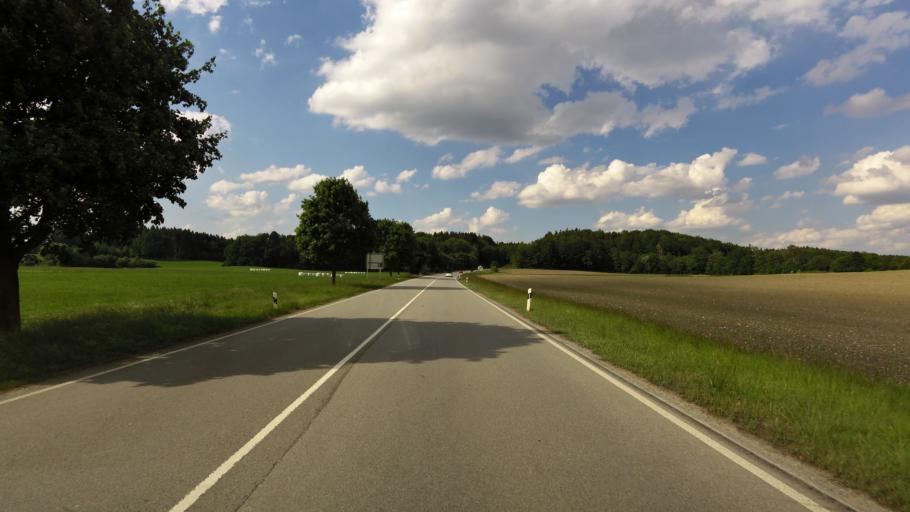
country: DE
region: Bavaria
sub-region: Upper Bavaria
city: Wasserburg am Inn
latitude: 48.0649
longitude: 12.1970
